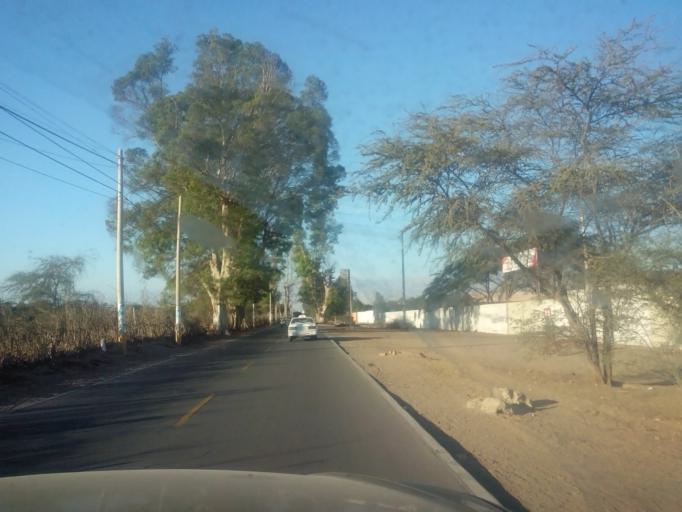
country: PE
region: Ica
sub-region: Provincia de Ica
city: Ica
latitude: -14.0838
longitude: -75.7533
